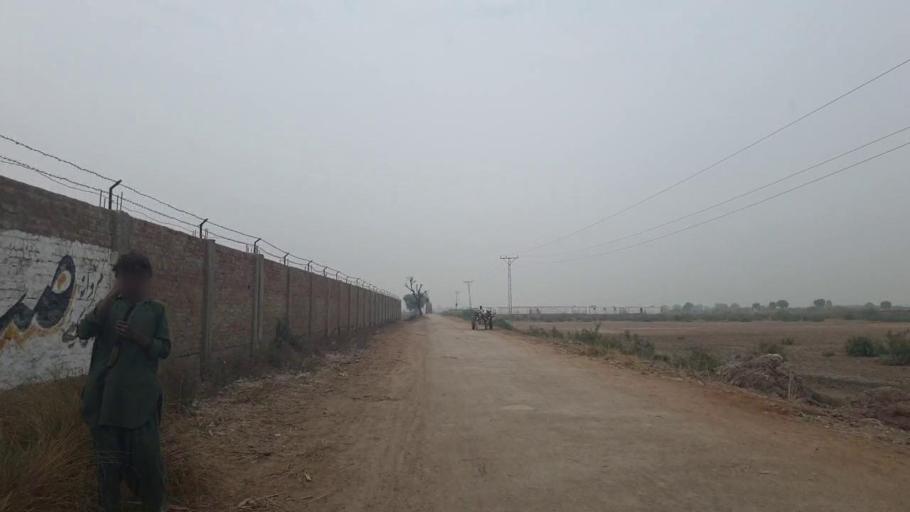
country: PK
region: Sindh
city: Tando Adam
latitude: 25.8018
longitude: 68.7222
